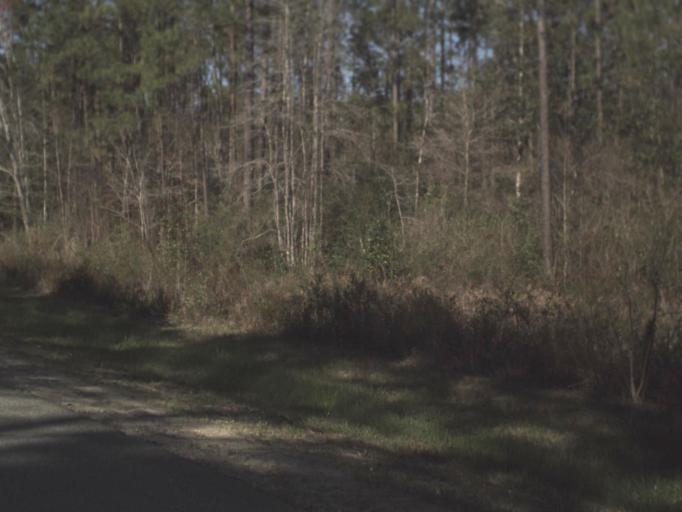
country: US
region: Florida
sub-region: Calhoun County
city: Blountstown
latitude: 30.4847
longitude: -85.1059
